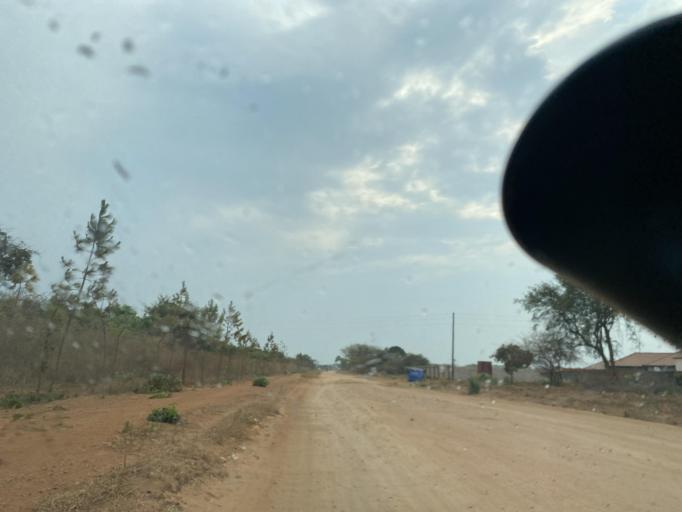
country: ZM
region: Lusaka
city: Lusaka
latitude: -15.2869
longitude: 28.2925
